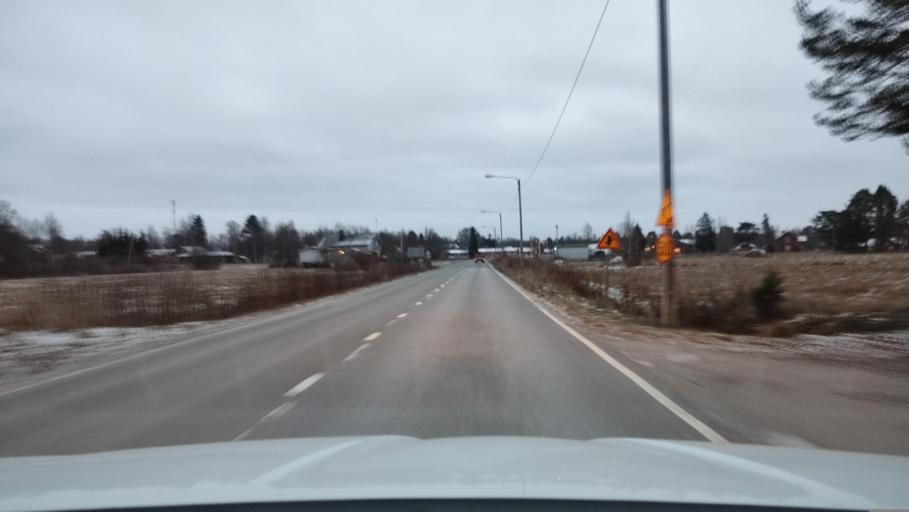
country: FI
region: Ostrobothnia
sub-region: Vaasa
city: Replot
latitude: 63.2341
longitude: 21.4043
